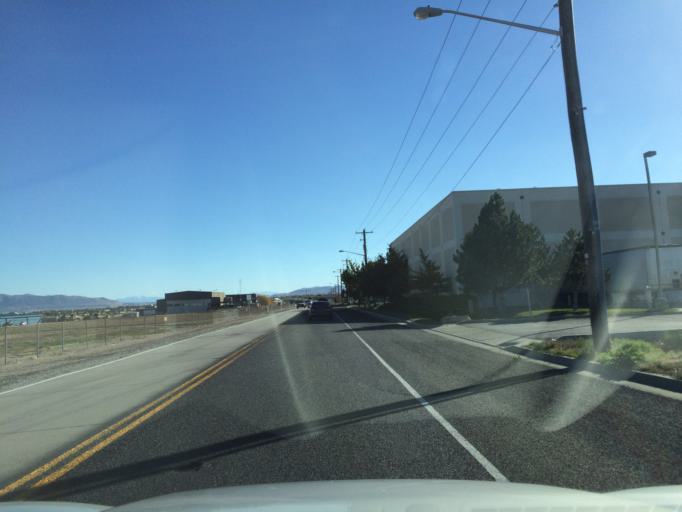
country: US
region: Utah
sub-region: Salt Lake County
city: Oquirrh
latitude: 40.6175
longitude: -111.9986
